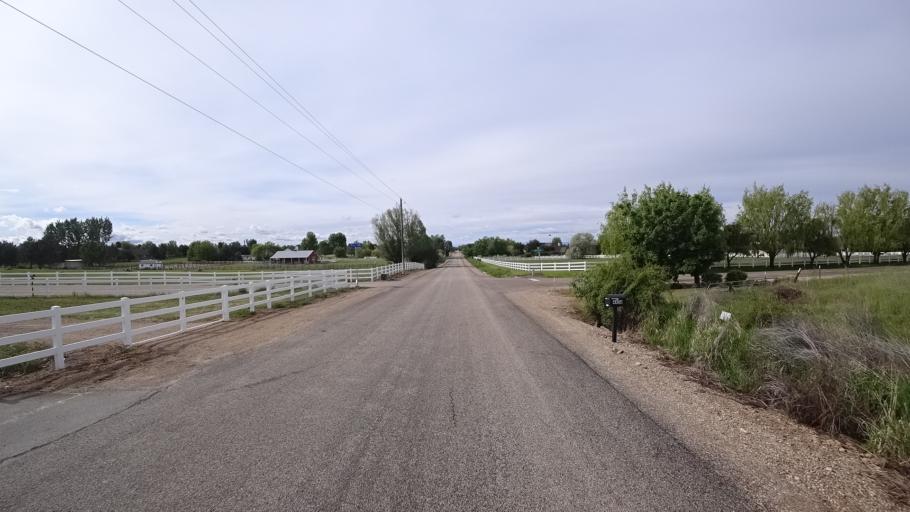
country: US
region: Idaho
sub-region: Ada County
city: Eagle
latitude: 43.7320
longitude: -116.4034
